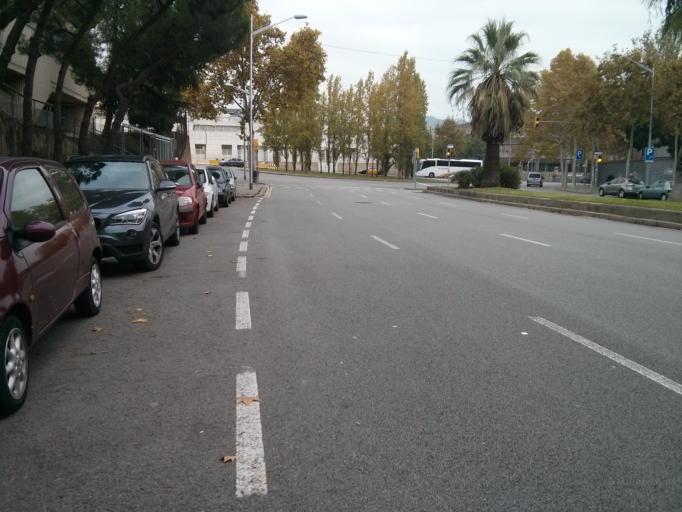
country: ES
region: Catalonia
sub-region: Provincia de Barcelona
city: les Corts
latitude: 41.3799
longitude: 2.1189
